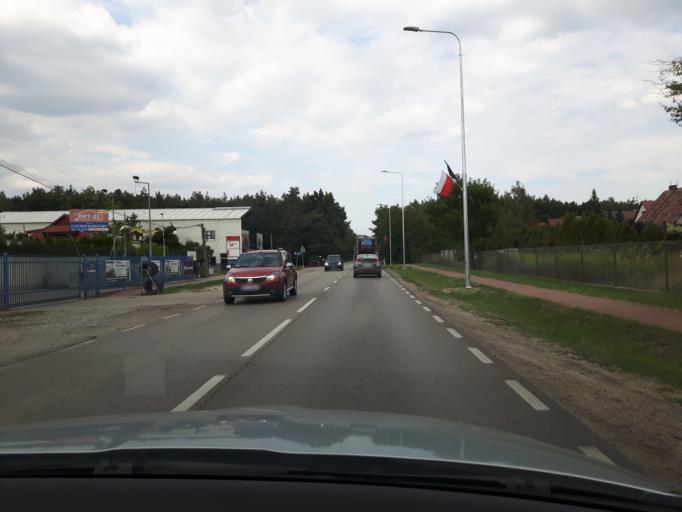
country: PL
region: Masovian Voivodeship
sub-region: Powiat legionowski
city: Stanislawow Pierwszy
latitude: 52.3988
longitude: 21.0359
